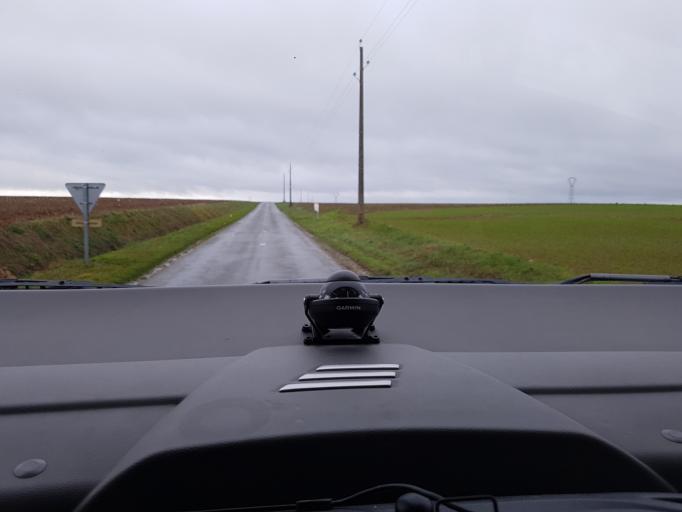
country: FR
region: Haute-Normandie
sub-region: Departement de l'Eure
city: Pont-Saint-Pierre
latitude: 49.3021
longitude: 1.3258
